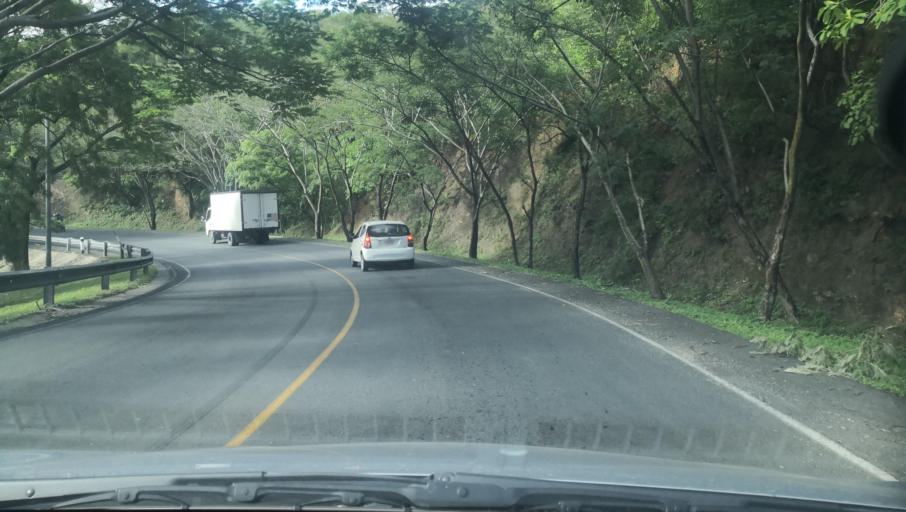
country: NI
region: Madriz
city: Totogalpa
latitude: 13.5940
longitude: -86.4721
